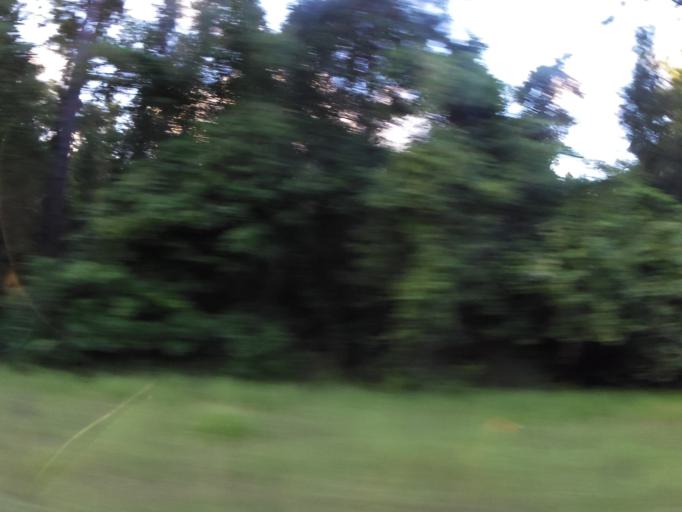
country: US
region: Georgia
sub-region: Camden County
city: Woodbine
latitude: 31.1068
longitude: -81.6547
